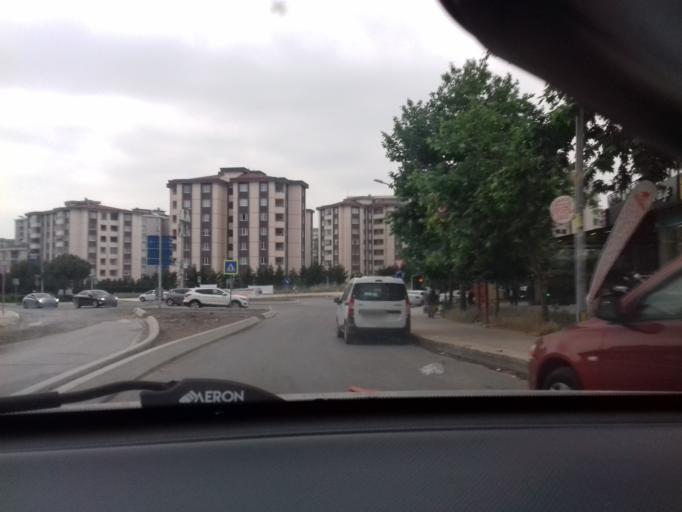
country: TR
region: Istanbul
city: Sultanbeyli
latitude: 40.9312
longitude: 29.2970
